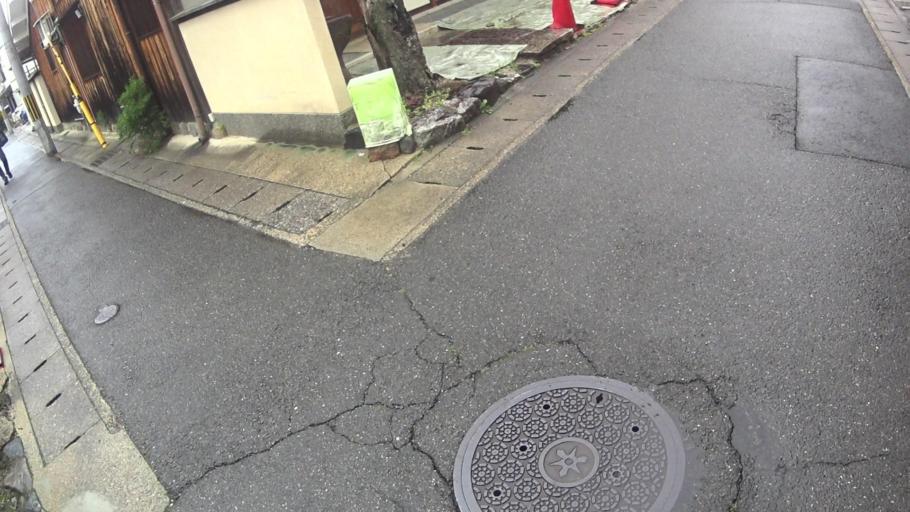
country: JP
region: Kyoto
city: Muko
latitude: 35.0145
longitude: 135.6844
